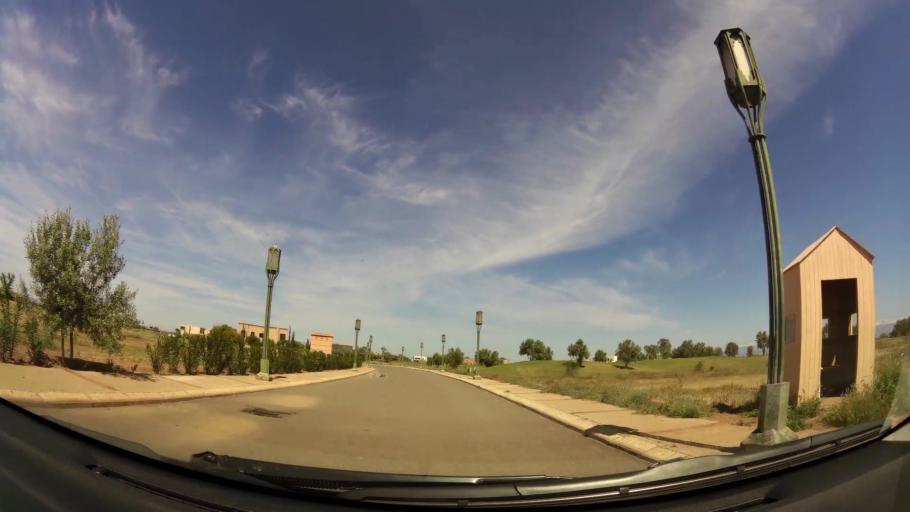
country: MA
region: Marrakech-Tensift-Al Haouz
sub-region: Marrakech
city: Marrakesh
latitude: 31.6171
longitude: -7.9257
